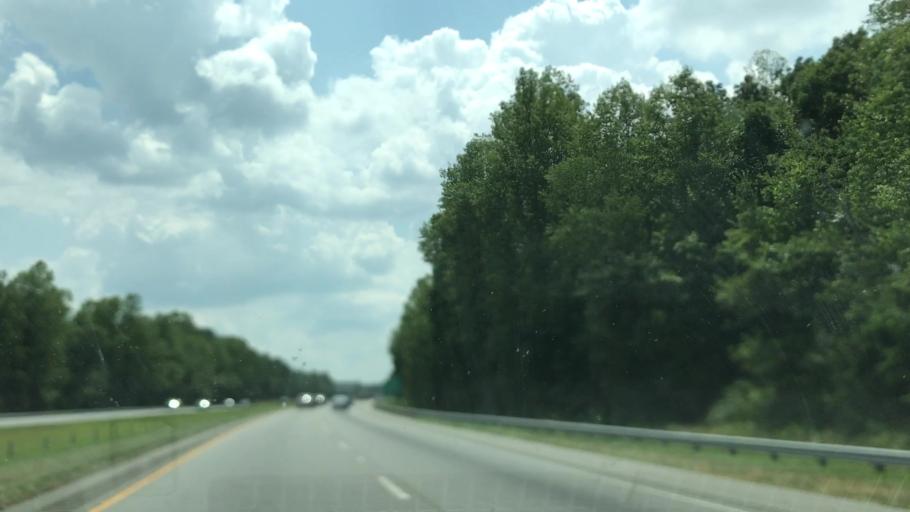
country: US
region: North Carolina
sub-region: Yadkin County
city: Yadkinville
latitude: 36.0260
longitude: -80.8216
